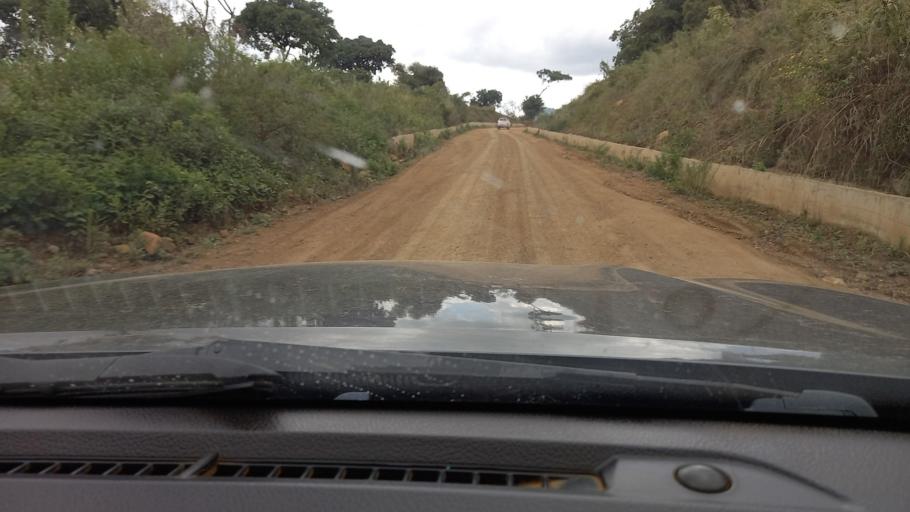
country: ET
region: Southern Nations, Nationalities, and People's Region
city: Mizan Teferi
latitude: 6.2047
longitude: 35.6568
